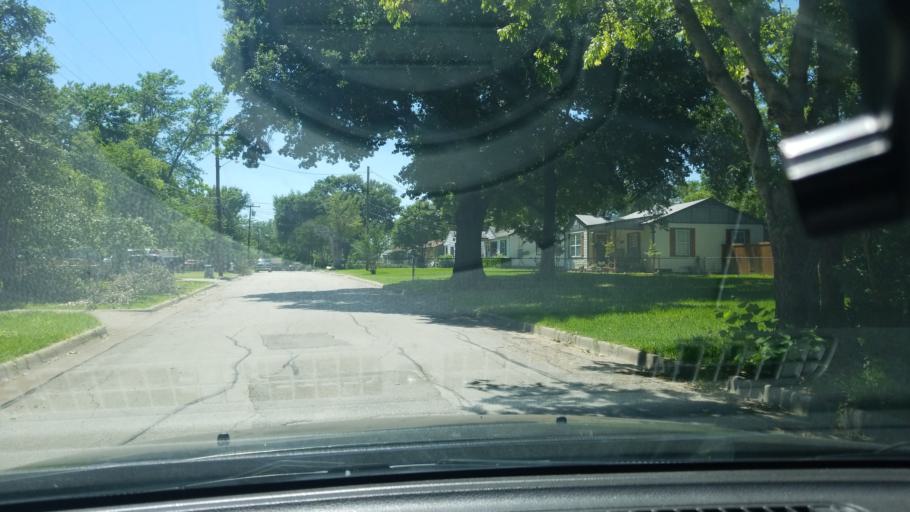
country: US
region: Texas
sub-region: Dallas County
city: Mesquite
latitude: 32.7627
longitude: -96.6070
